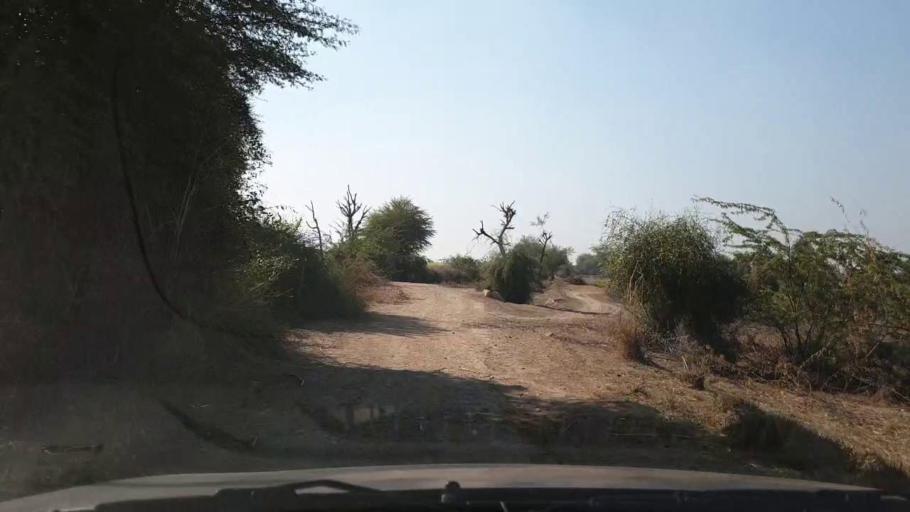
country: PK
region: Sindh
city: Jhol
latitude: 25.9214
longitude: 68.7939
